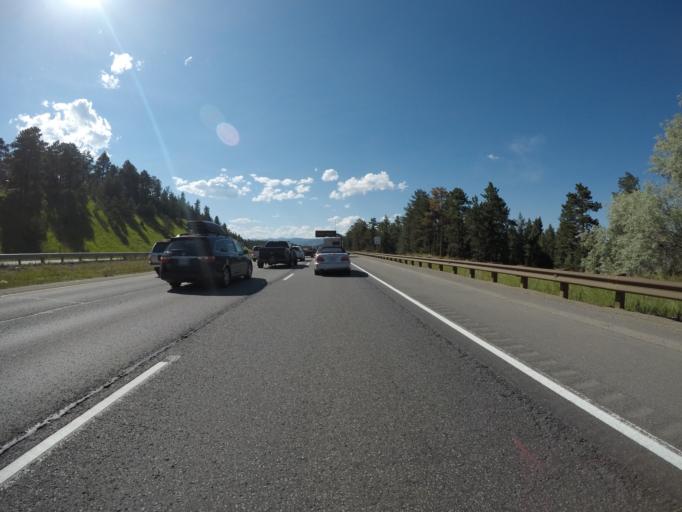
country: US
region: Colorado
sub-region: Jefferson County
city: Kittredge
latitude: 39.7082
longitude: -105.3471
